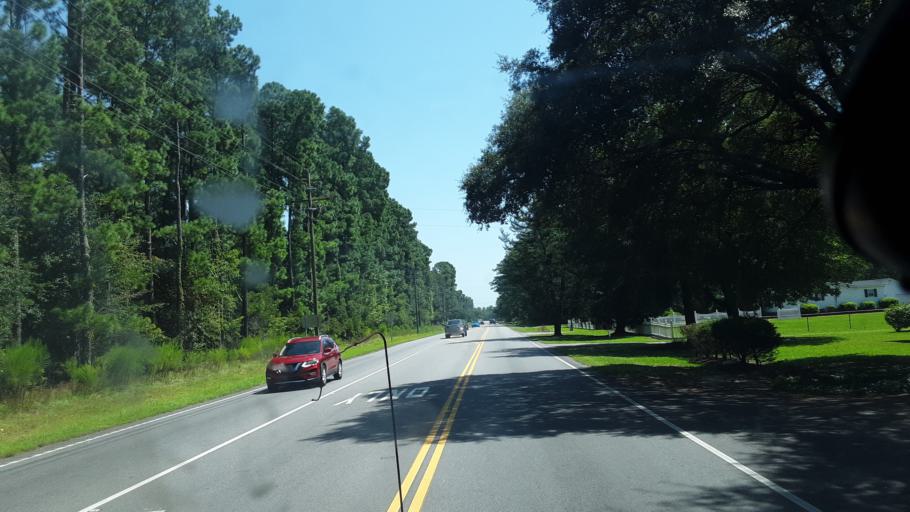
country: US
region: South Carolina
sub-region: Horry County
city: Red Hill
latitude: 33.8221
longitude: -78.9138
